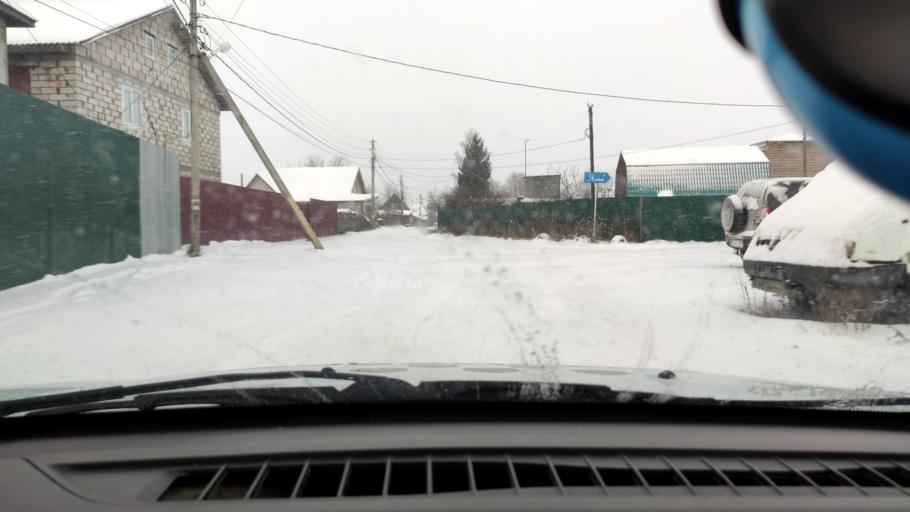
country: RU
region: Perm
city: Kondratovo
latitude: 58.0145
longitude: 56.0487
